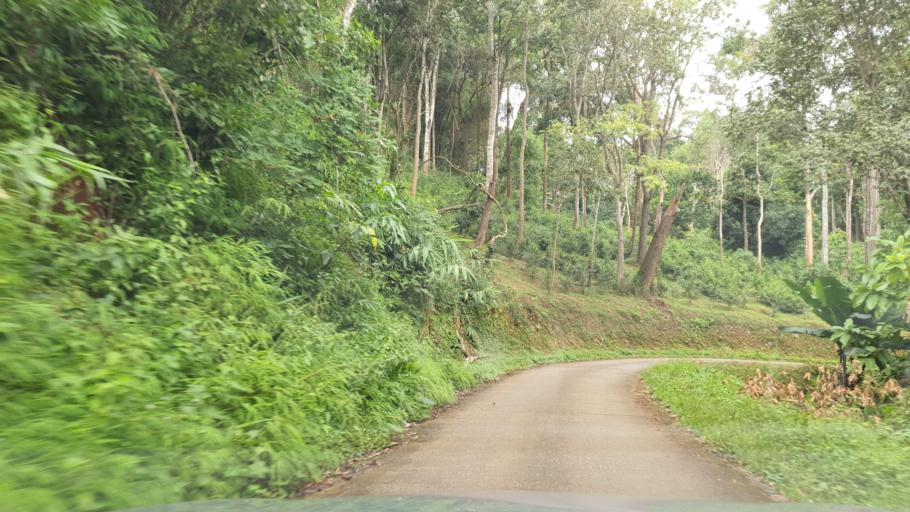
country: TH
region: Chiang Mai
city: Mae Taeng
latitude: 19.2354
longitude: 98.9317
